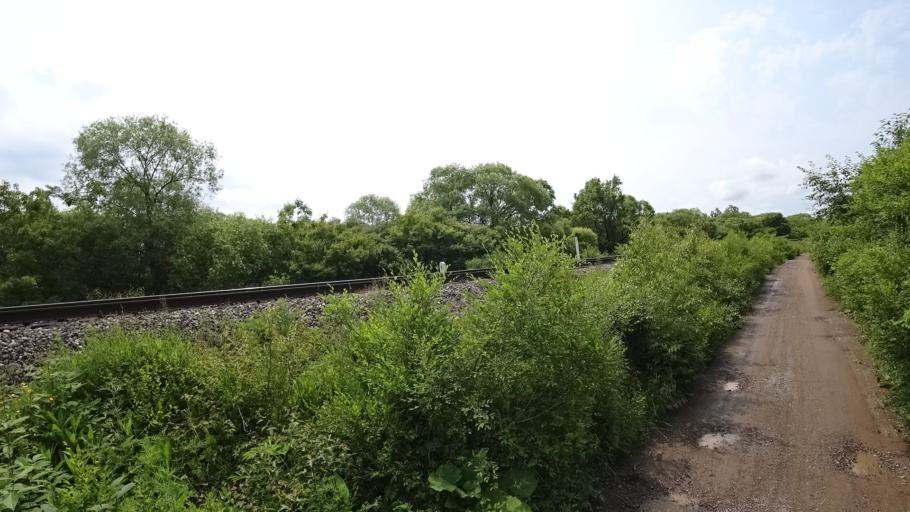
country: RU
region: Primorskiy
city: Novosysoyevka
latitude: 44.2492
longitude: 133.3729
